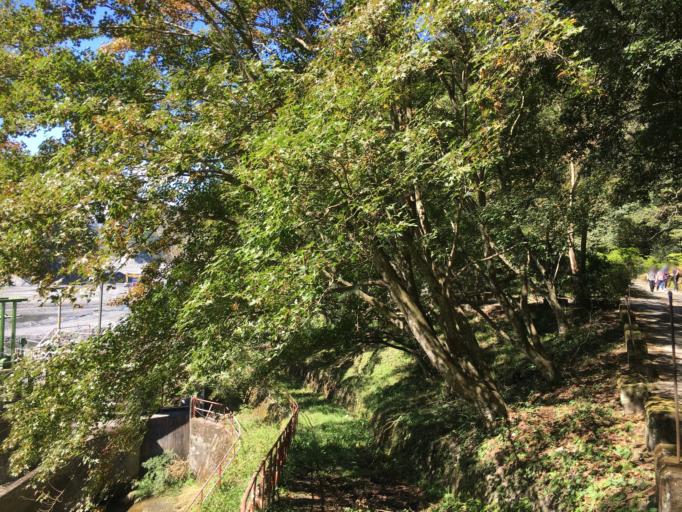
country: TW
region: Taiwan
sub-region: Nantou
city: Puli
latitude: 23.9501
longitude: 121.1829
